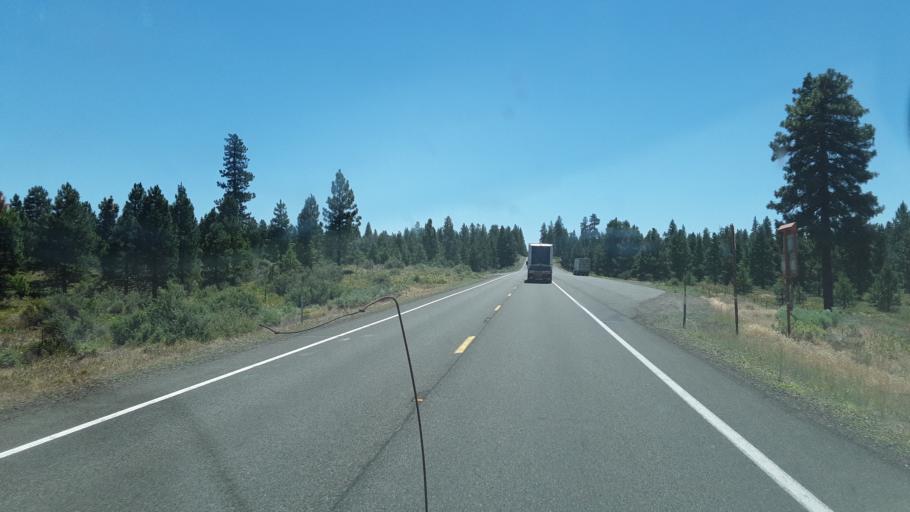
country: US
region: California
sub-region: Siskiyou County
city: Tulelake
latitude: 41.5746
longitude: -121.1840
